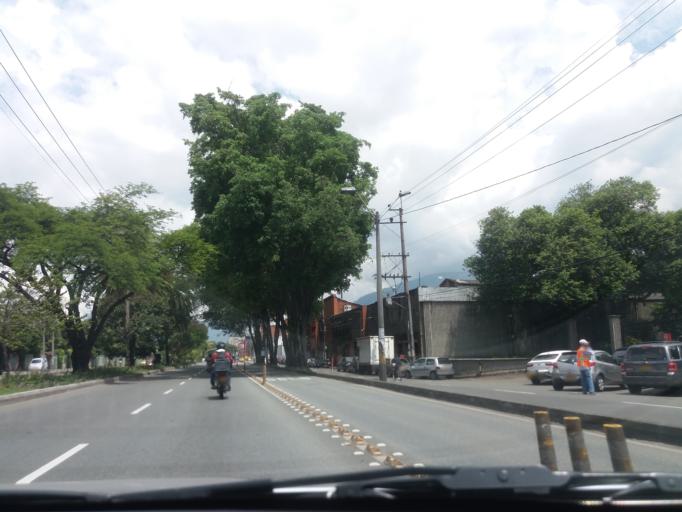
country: CO
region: Antioquia
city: Medellin
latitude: 6.2236
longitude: -75.5793
